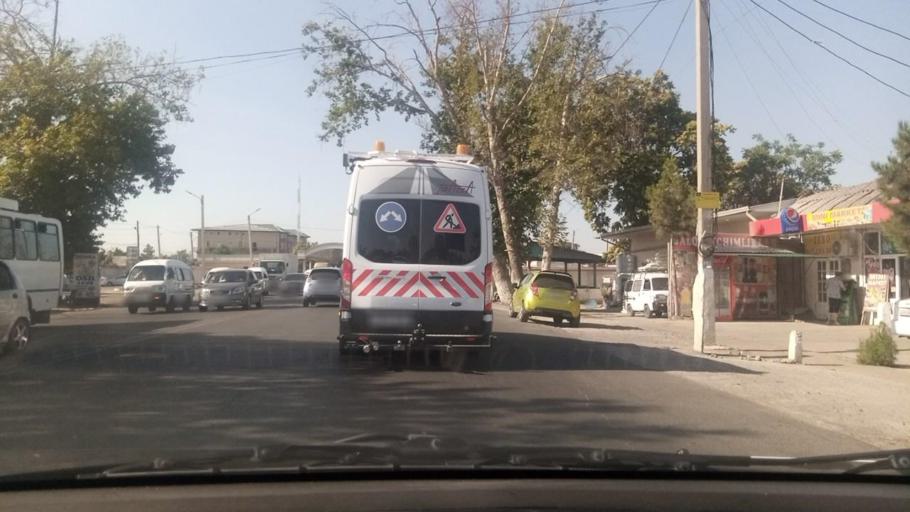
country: UZ
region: Toshkent Shahri
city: Bektemir
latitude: 41.2273
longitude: 69.3356
